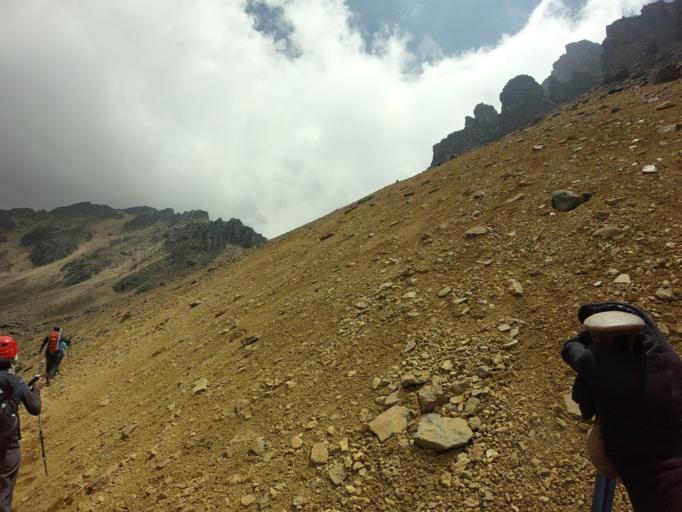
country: MX
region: Mexico
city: Amecameca de Juarez
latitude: 19.1474
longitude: -98.6379
